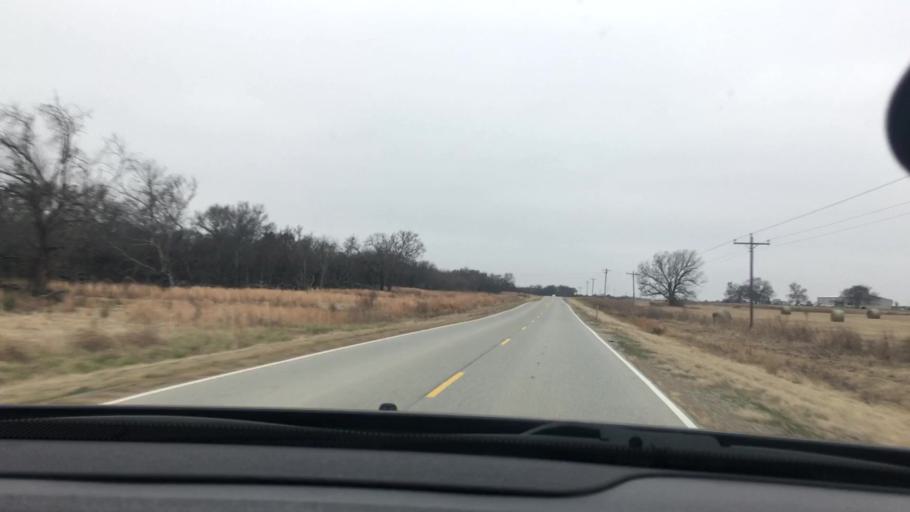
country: US
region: Oklahoma
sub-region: Coal County
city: Coalgate
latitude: 34.5133
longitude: -96.2887
